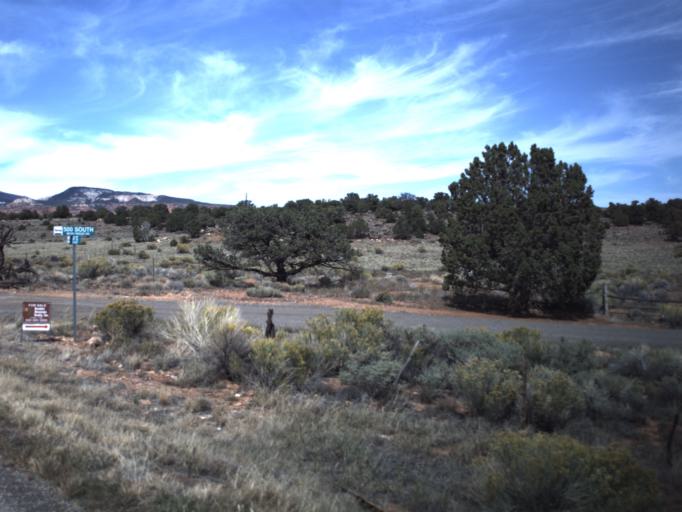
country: US
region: Utah
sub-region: Wayne County
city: Loa
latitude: 38.2907
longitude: -111.3954
